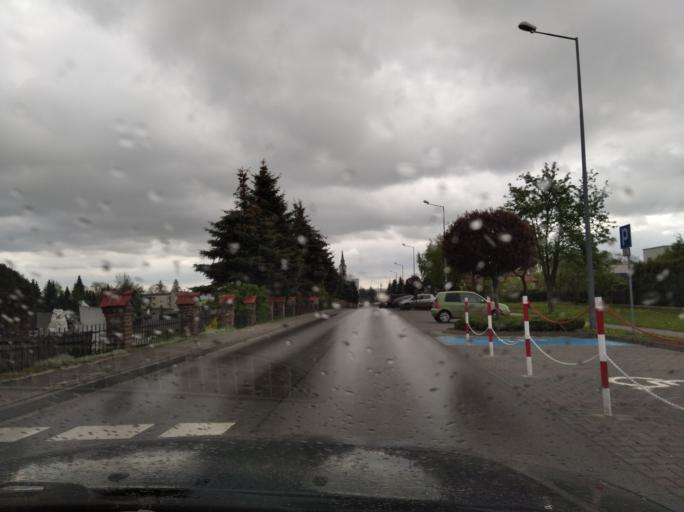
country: PL
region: Subcarpathian Voivodeship
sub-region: Powiat rzeszowski
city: Boguchwala
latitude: 49.9859
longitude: 21.9422
